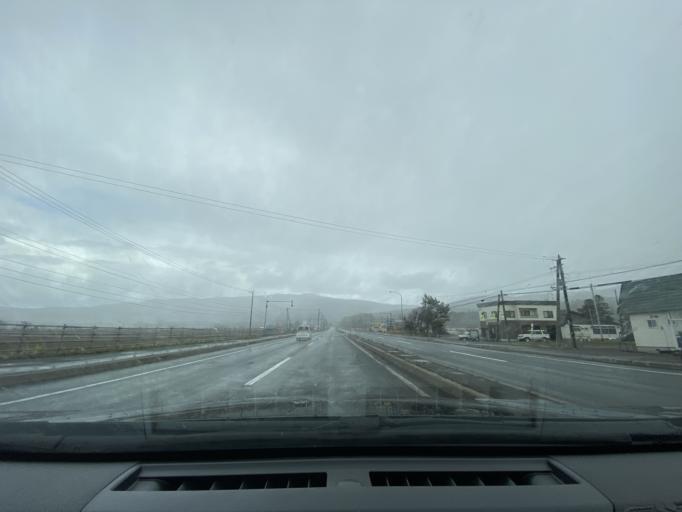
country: JP
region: Hokkaido
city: Fukagawa
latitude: 43.7212
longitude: 142.1833
